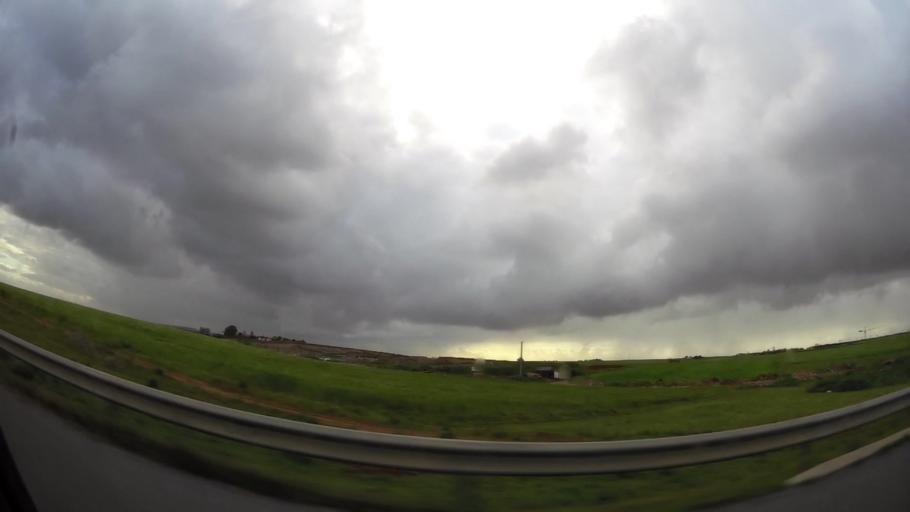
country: MA
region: Grand Casablanca
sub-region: Mediouna
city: Tit Mellil
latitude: 33.6075
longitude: -7.4357
